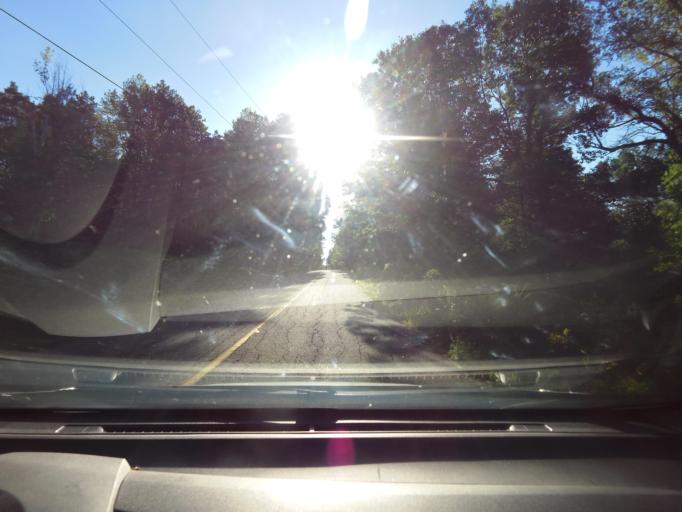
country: CA
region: Quebec
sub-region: Mauricie
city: Becancour
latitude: 46.5520
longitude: -72.3876
